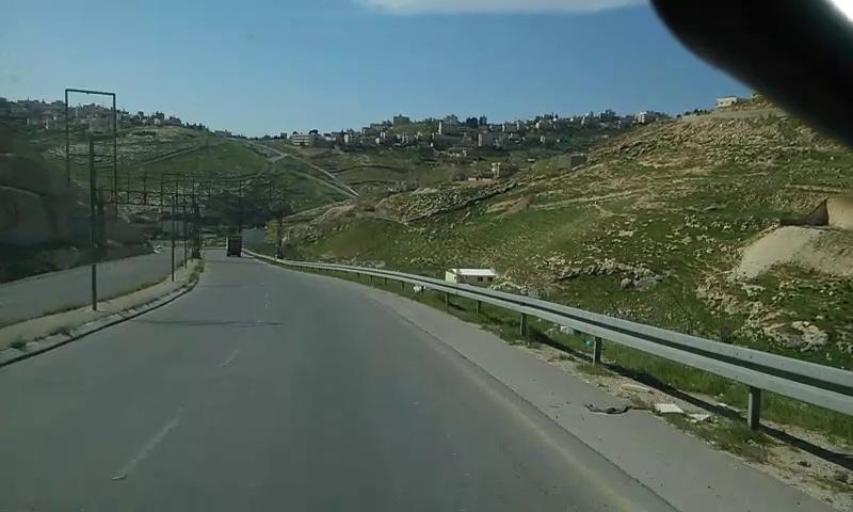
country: PS
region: West Bank
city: Abu Dis
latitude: 31.7486
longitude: 35.2784
